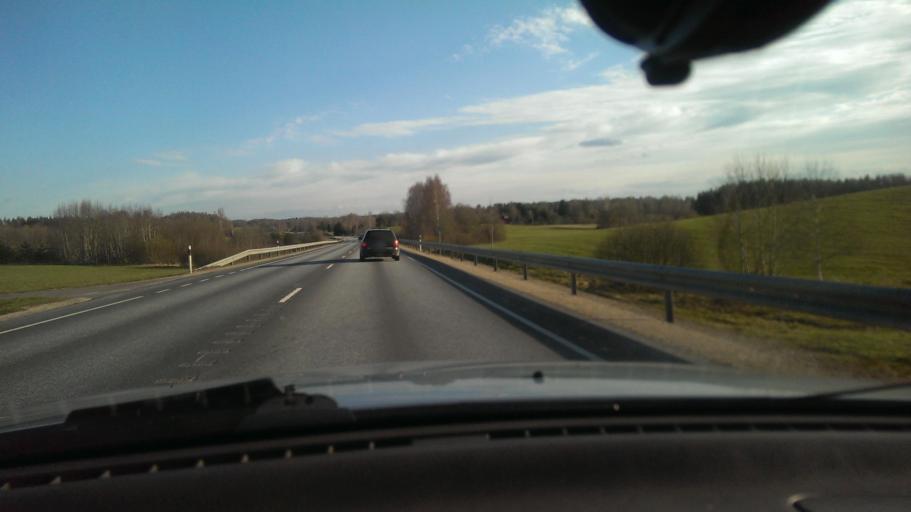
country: EE
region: Tartu
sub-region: UElenurme vald
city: Ulenurme
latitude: 58.1781
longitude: 26.6918
